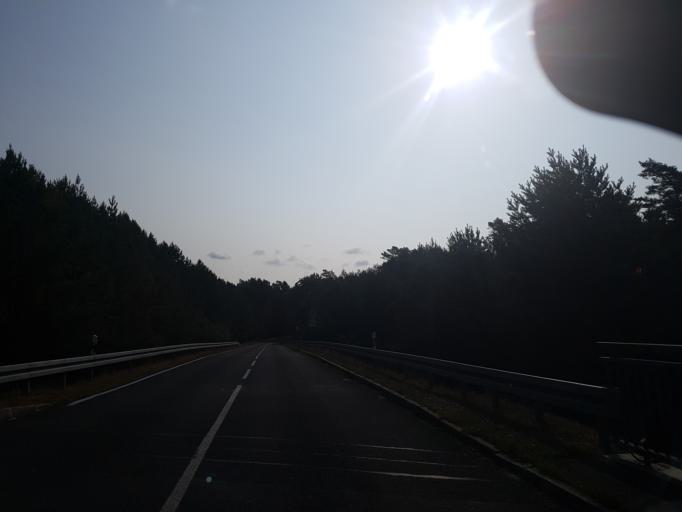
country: DE
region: Brandenburg
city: Wiesenburg
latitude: 52.0761
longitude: 12.3984
